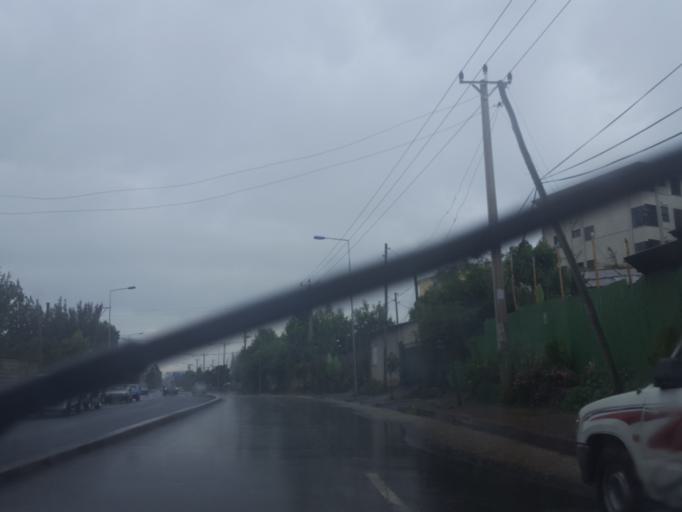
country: ET
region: Adis Abeba
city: Addis Ababa
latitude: 9.0278
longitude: 38.7787
